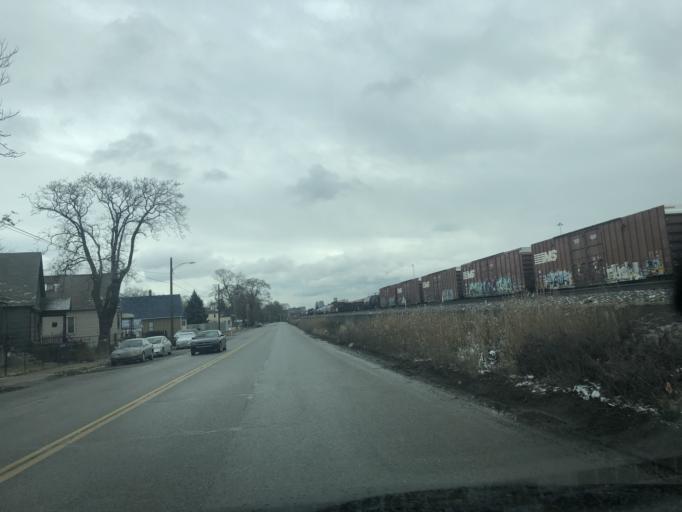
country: US
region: Michigan
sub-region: Wayne County
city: River Rouge
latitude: 42.3234
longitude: -83.1217
